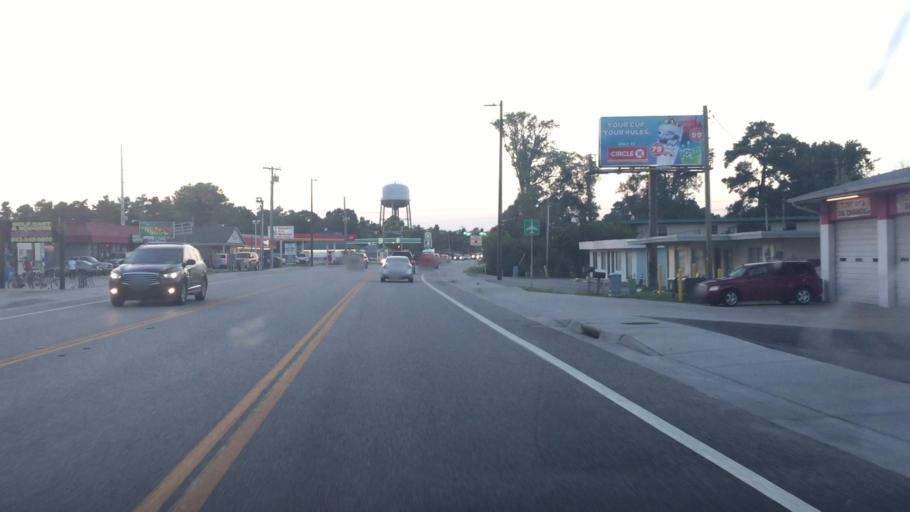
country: US
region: South Carolina
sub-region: Horry County
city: Myrtle Beach
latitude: 33.6897
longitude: -78.8955
